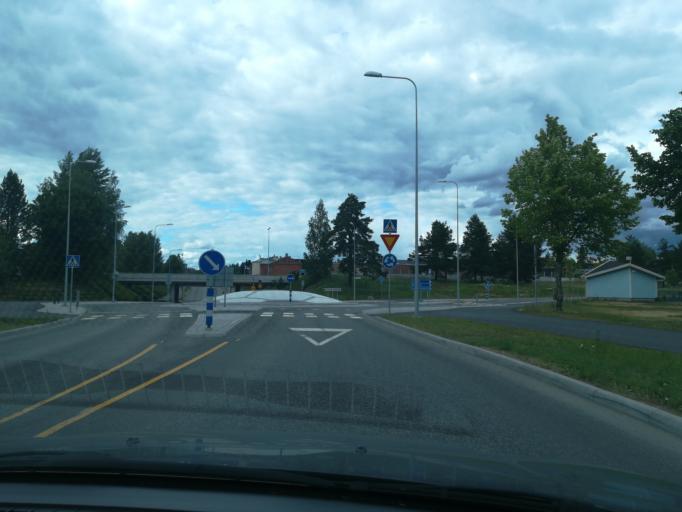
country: FI
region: Southern Savonia
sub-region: Mikkeli
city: Mikkeli
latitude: 61.6773
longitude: 27.2570
